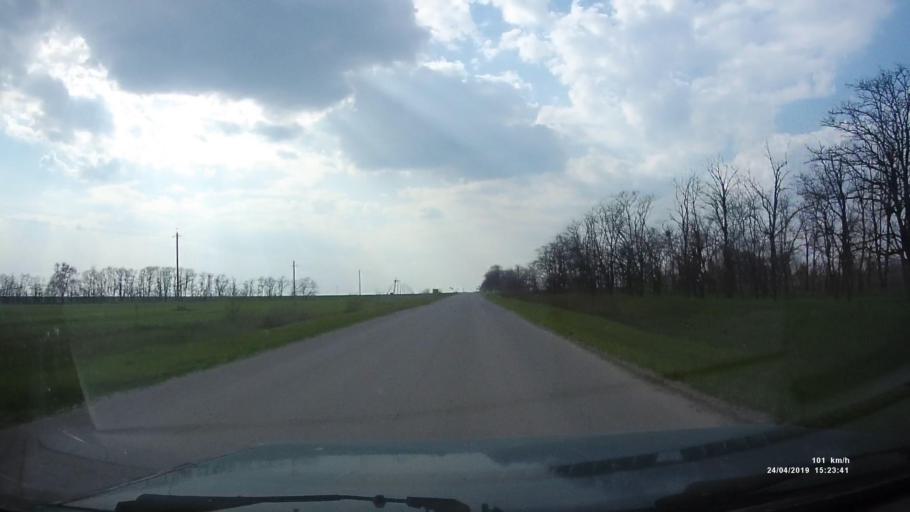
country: RU
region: Rostov
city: Remontnoye
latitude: 46.5445
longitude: 43.0846
